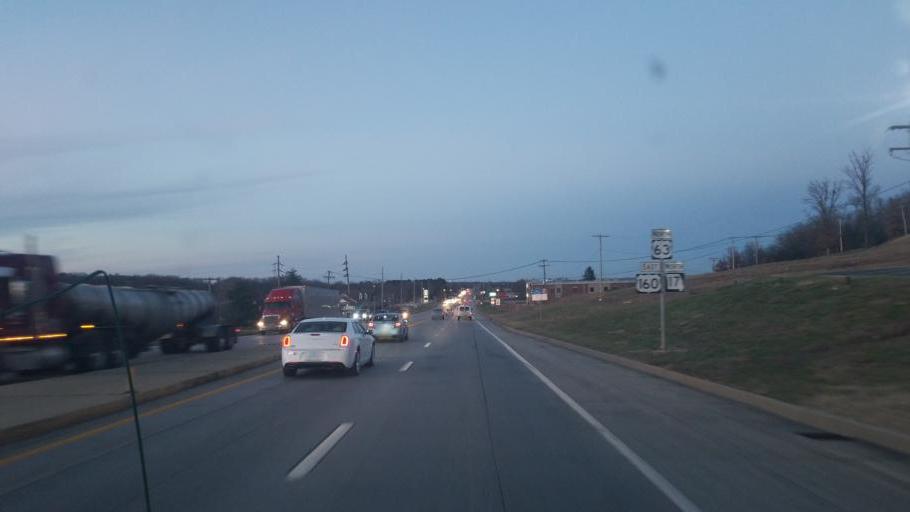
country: US
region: Missouri
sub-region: Howell County
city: West Plains
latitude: 36.7267
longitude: -91.8773
